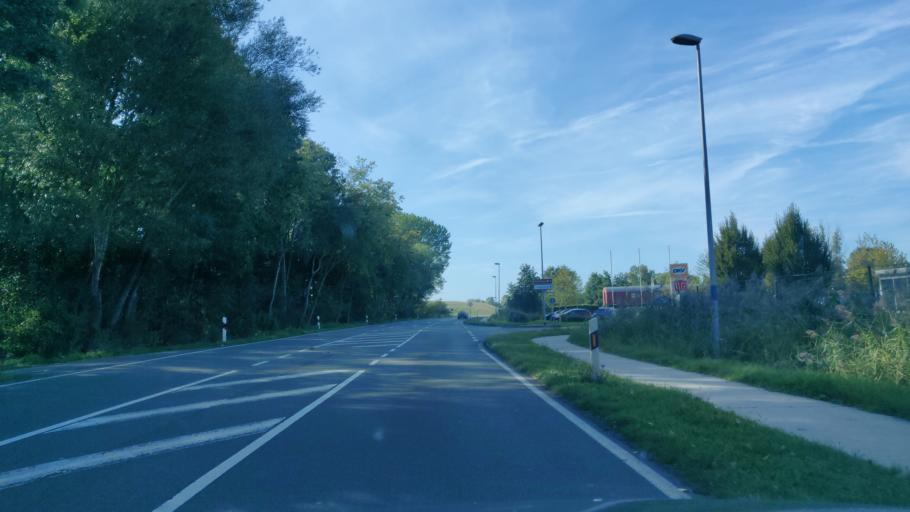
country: DE
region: Lower Saxony
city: Leer
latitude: 53.2307
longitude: 7.4296
